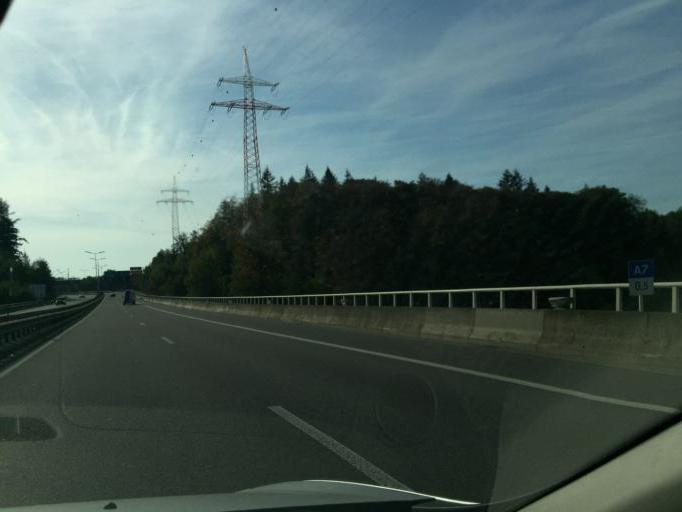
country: LU
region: Luxembourg
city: Kirchberg
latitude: 49.6451
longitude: 6.1878
